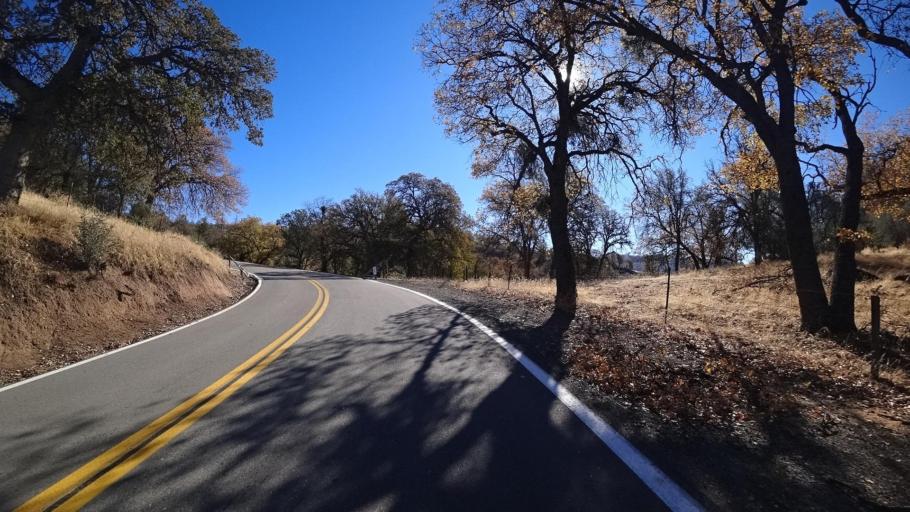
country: US
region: California
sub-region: Kern County
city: Alta Sierra
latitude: 35.7370
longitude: -118.6198
